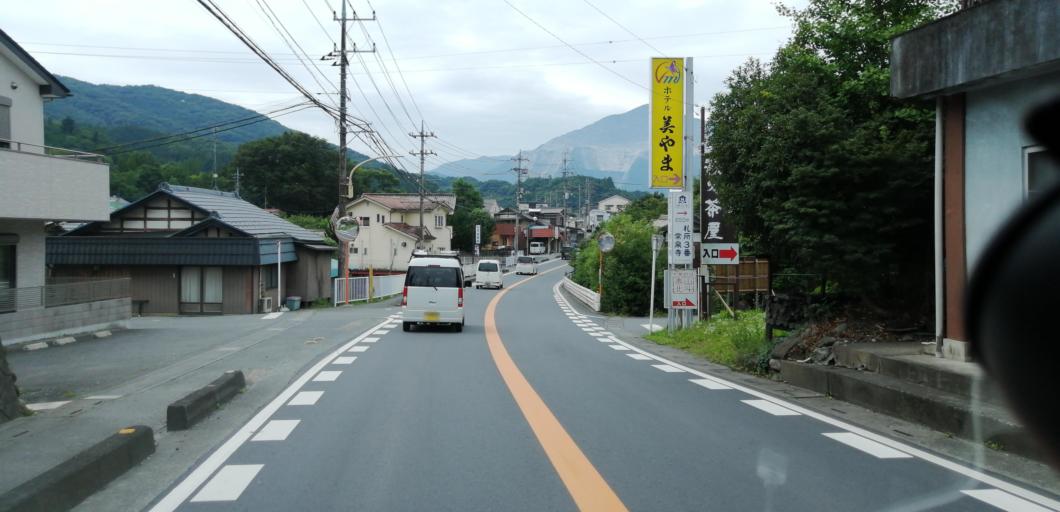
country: JP
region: Saitama
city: Chichibu
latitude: 36.0136
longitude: 139.1122
